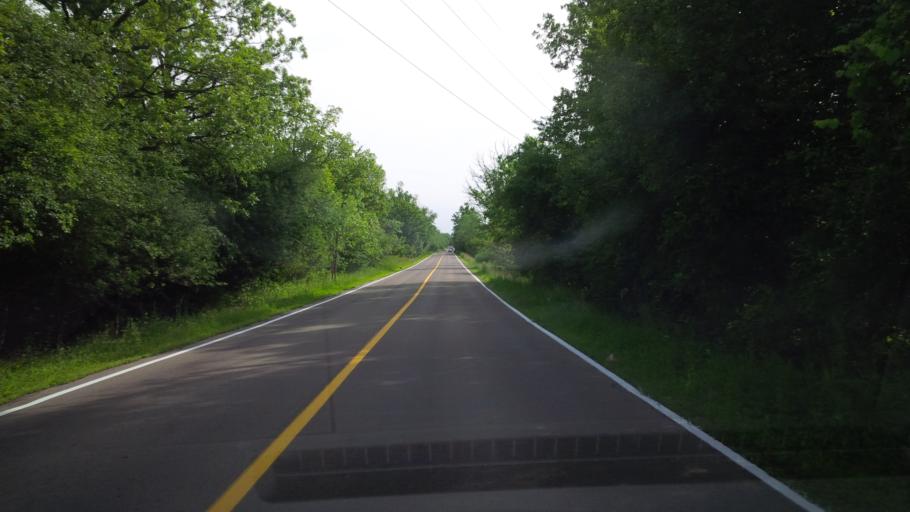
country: CA
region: Ontario
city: Burlington
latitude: 43.3379
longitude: -79.8726
